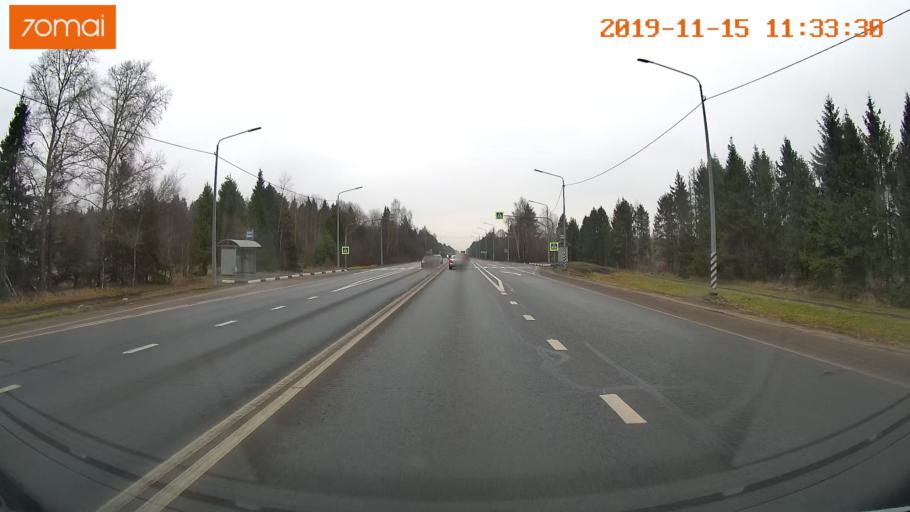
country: RU
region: Vologda
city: Molochnoye
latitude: 59.1894
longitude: 39.5929
